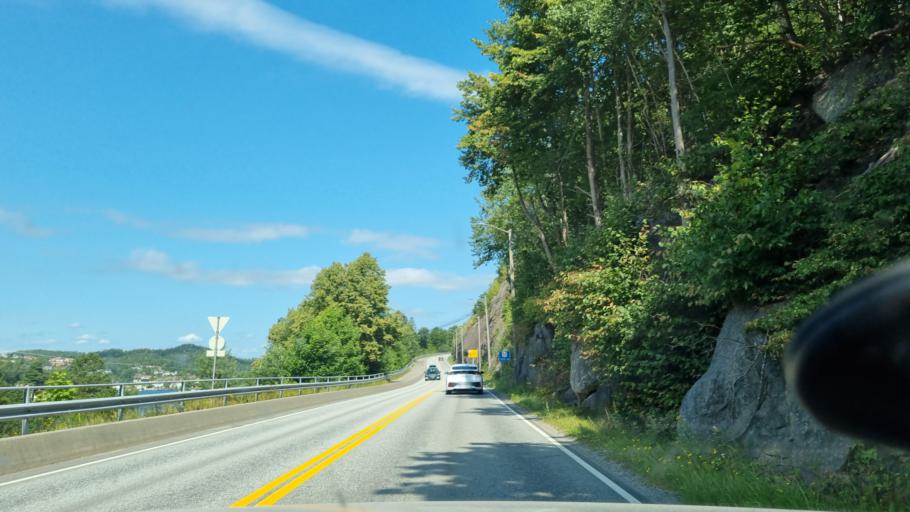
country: NO
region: Aust-Agder
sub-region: Arendal
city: Arendal
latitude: 58.4601
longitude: 8.8192
